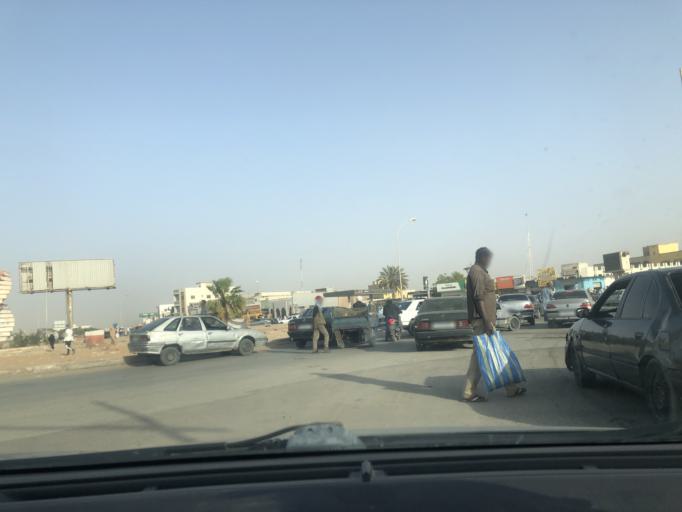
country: MR
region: Nouakchott
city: Nouakchott
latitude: 18.0791
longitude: -15.9658
